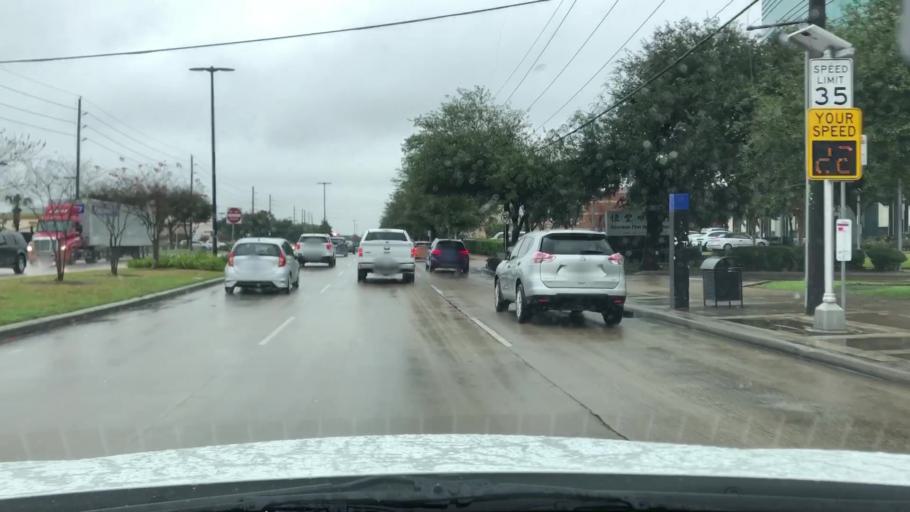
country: US
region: Texas
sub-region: Fort Bend County
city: Meadows Place
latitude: 29.7045
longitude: -95.5562
